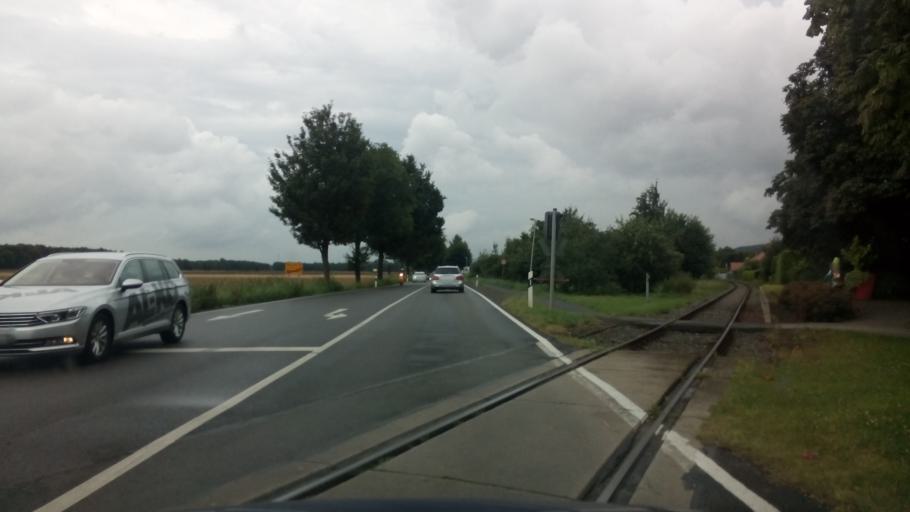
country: DE
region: Lower Saxony
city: Bad Essen
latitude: 52.3317
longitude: 8.3163
